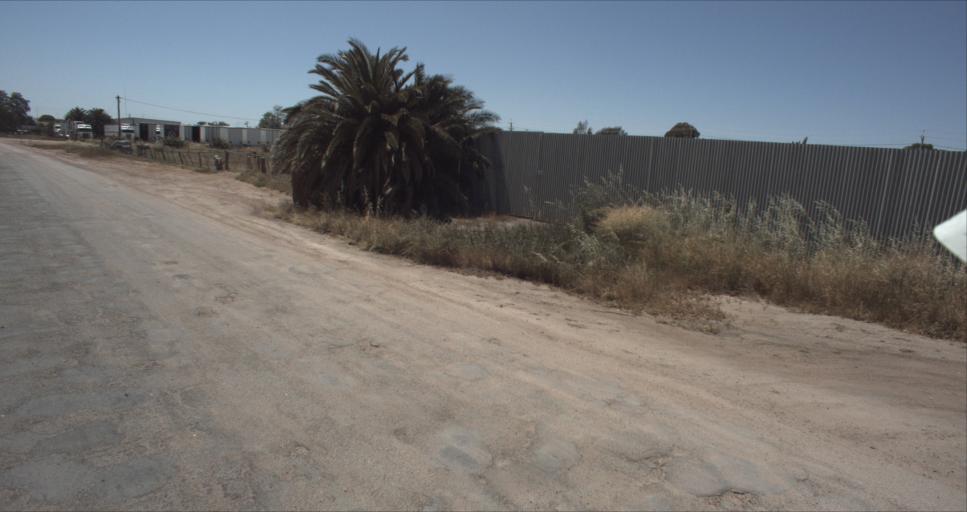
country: AU
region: New South Wales
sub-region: Leeton
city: Leeton
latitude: -34.5491
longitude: 146.3968
